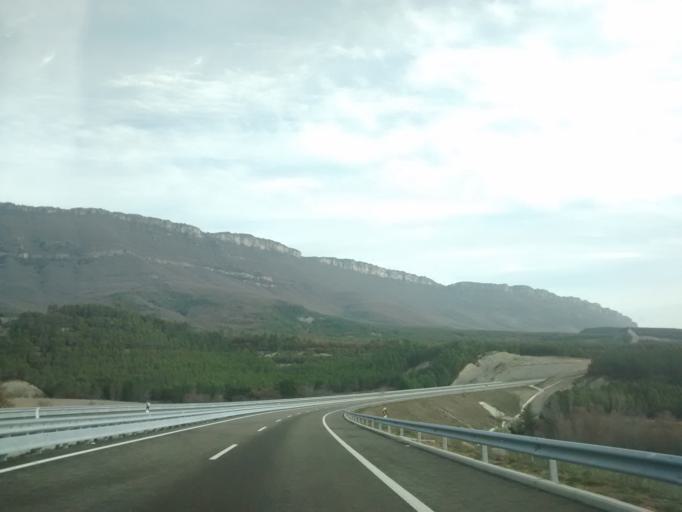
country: ES
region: Aragon
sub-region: Provincia de Zaragoza
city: Undues de Lerda
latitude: 42.6215
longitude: -1.1376
